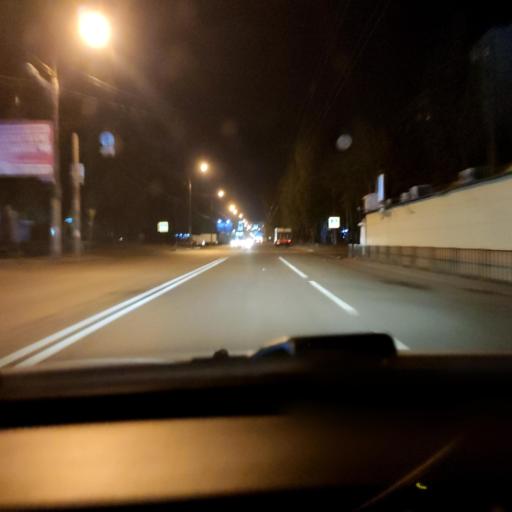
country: RU
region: Voronezj
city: Podgornoye
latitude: 51.7080
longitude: 39.1741
